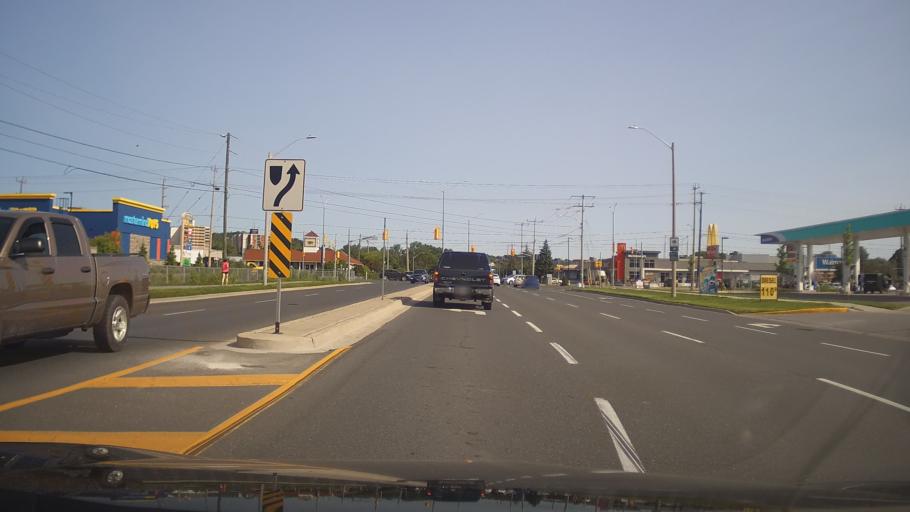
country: CA
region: Ontario
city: Peterborough
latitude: 44.2813
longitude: -78.3433
